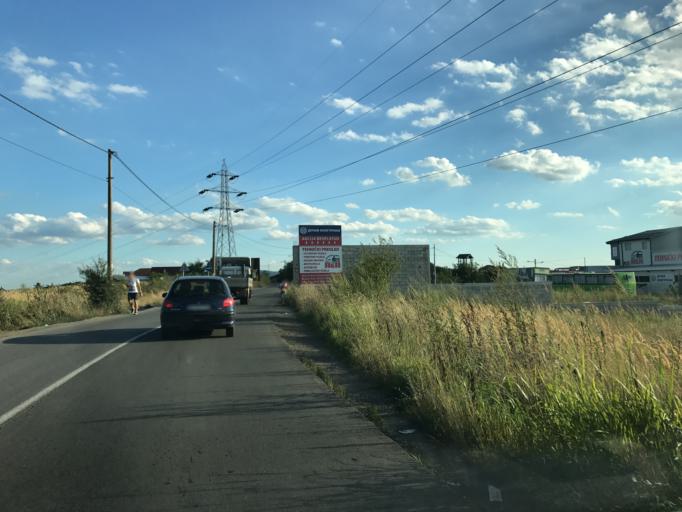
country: RS
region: Central Serbia
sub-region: Belgrade
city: Zvezdara
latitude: 44.7810
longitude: 20.5479
